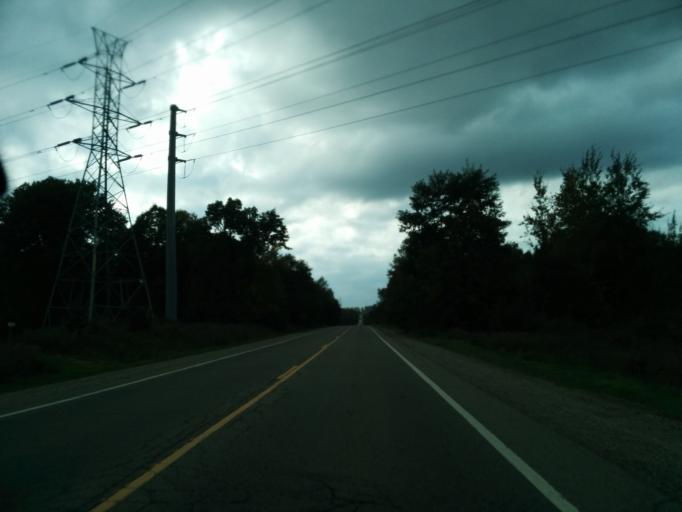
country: US
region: Michigan
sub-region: Oakland County
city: Waterford
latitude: 42.6935
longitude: -83.4858
